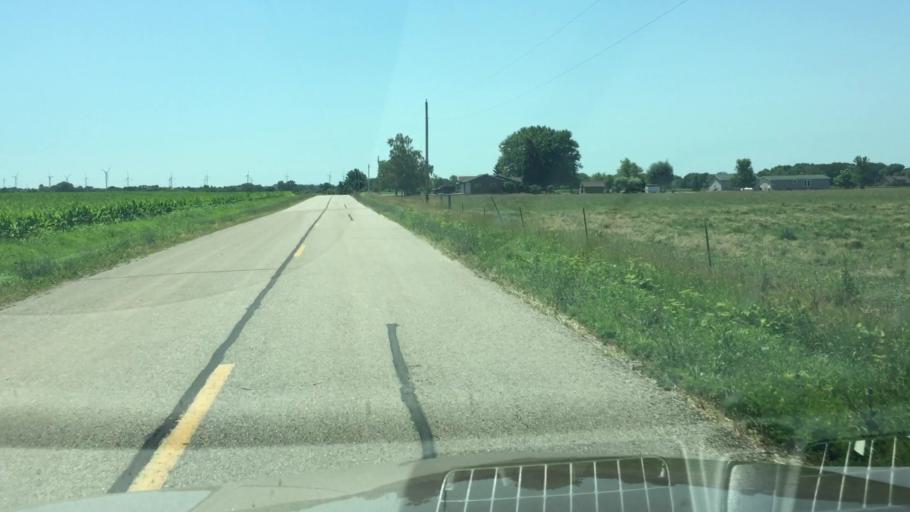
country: US
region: Wisconsin
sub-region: Fond du Lac County
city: Saint Peter
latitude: 43.9502
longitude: -88.3115
